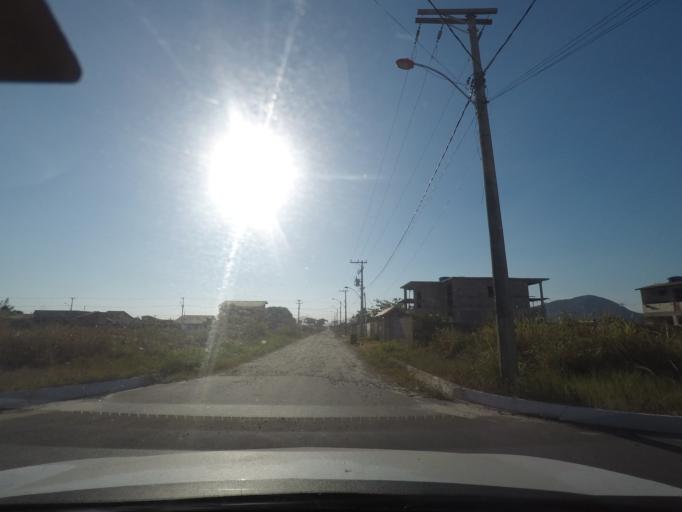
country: BR
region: Rio de Janeiro
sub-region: Marica
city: Marica
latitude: -22.9619
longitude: -42.9271
